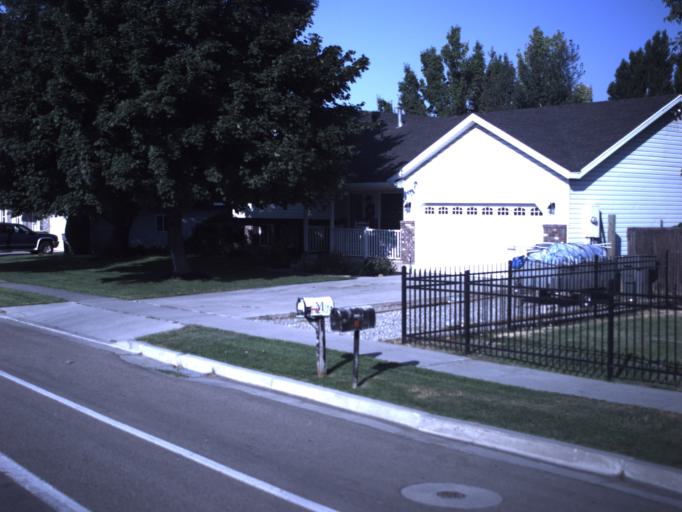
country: US
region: Utah
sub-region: Utah County
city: American Fork
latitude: 40.4021
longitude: -111.7932
